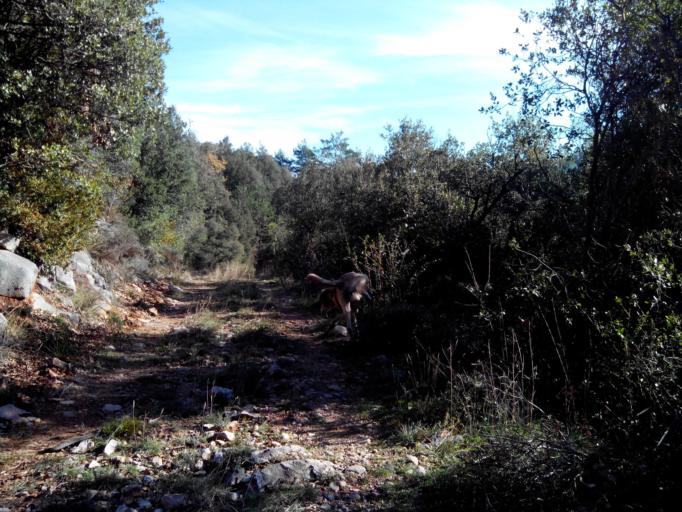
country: ES
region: Catalonia
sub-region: Provincia de Barcelona
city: Vilada
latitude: 42.1071
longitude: 1.9388
